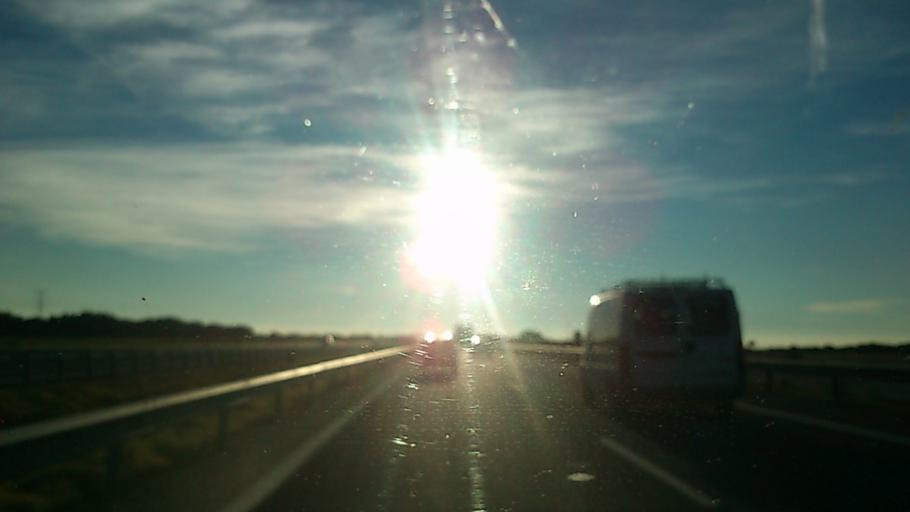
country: ES
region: Castille-La Mancha
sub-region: Provincia de Guadalajara
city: Utande
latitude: 40.8230
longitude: -2.9210
